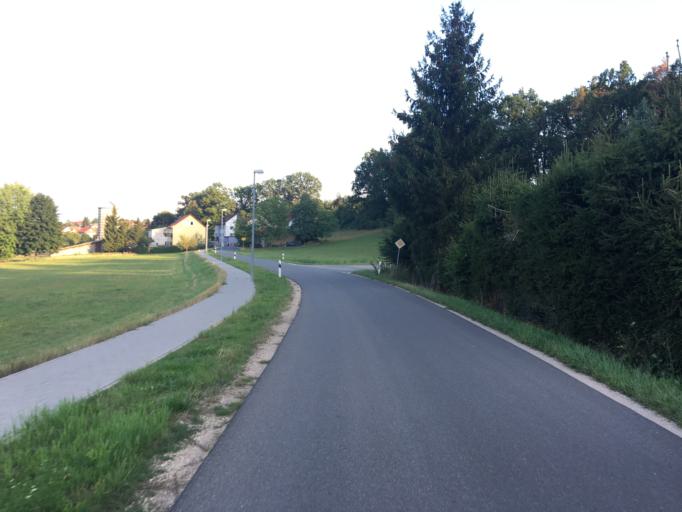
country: DE
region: Bavaria
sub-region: Regierungsbezirk Mittelfranken
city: Wilhermsdorf
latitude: 49.4866
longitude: 10.7035
